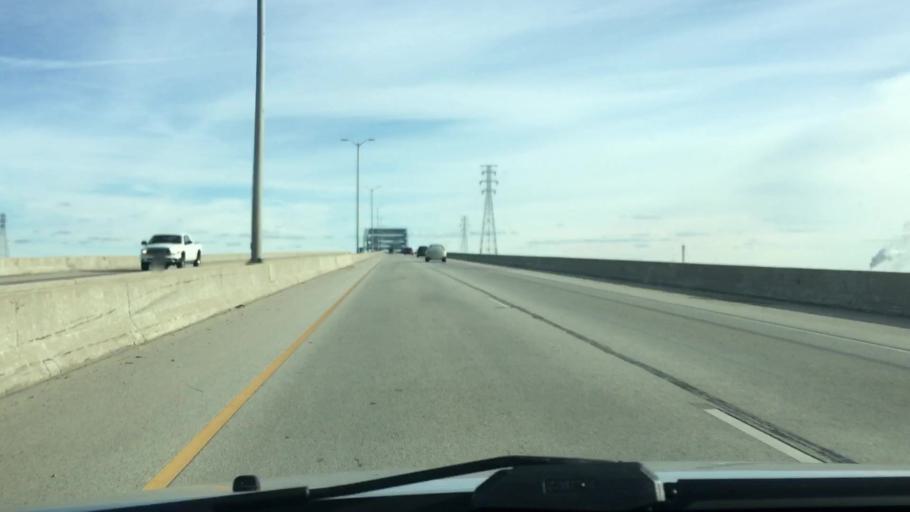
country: US
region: Wisconsin
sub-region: Brown County
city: Green Bay
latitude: 44.5356
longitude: -88.0153
